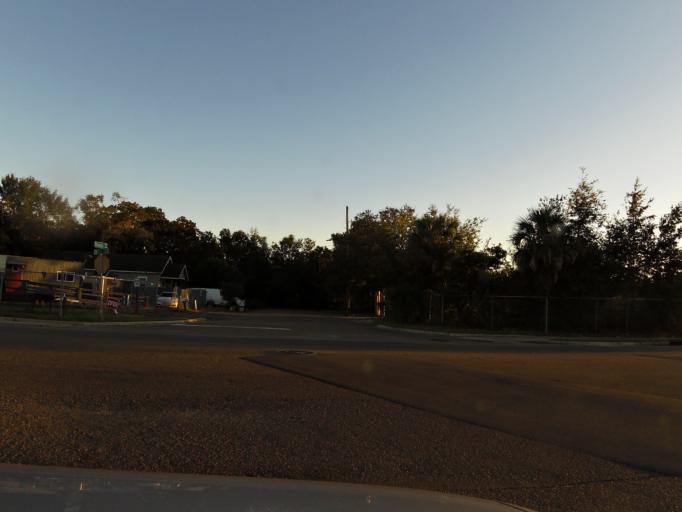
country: US
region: Florida
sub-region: Duval County
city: Jacksonville
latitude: 30.3453
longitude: -81.6410
